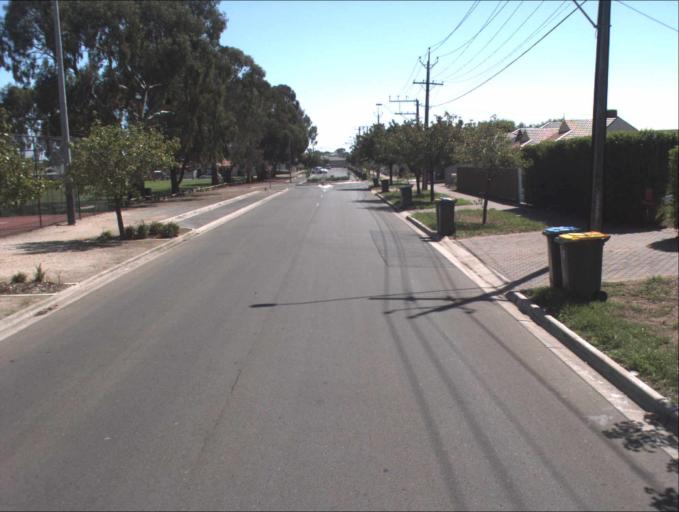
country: AU
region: South Australia
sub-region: Port Adelaide Enfield
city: Klemzig
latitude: -34.8685
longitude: 138.6245
